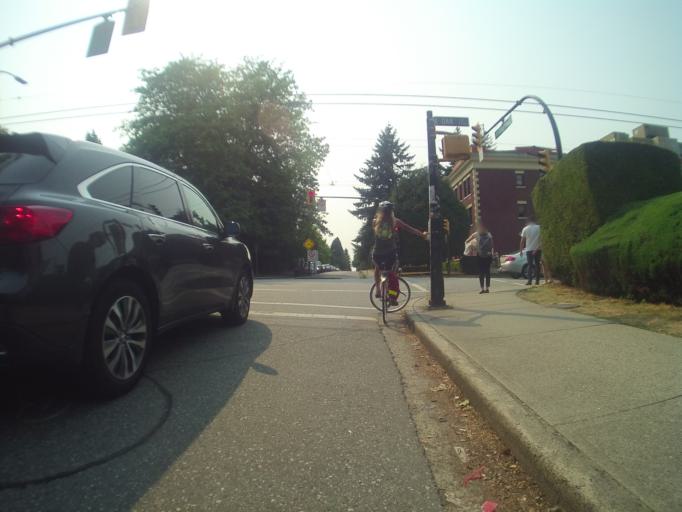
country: CA
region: British Columbia
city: Vancouver
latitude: 49.2625
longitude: -123.1263
